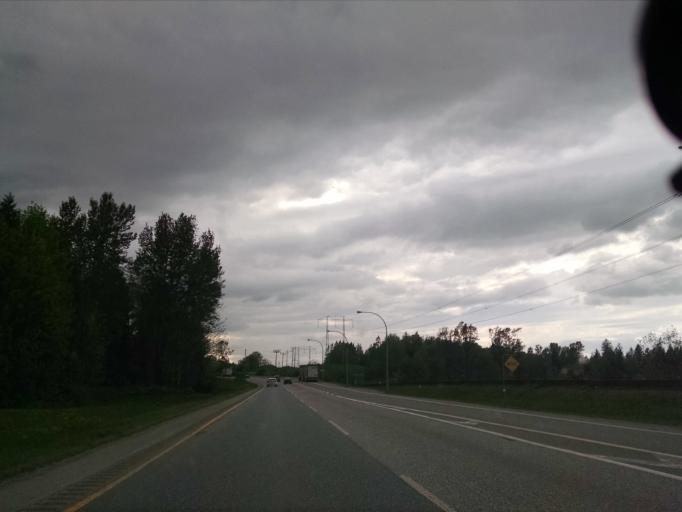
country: CA
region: British Columbia
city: Agassiz
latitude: 49.1968
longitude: -121.7322
